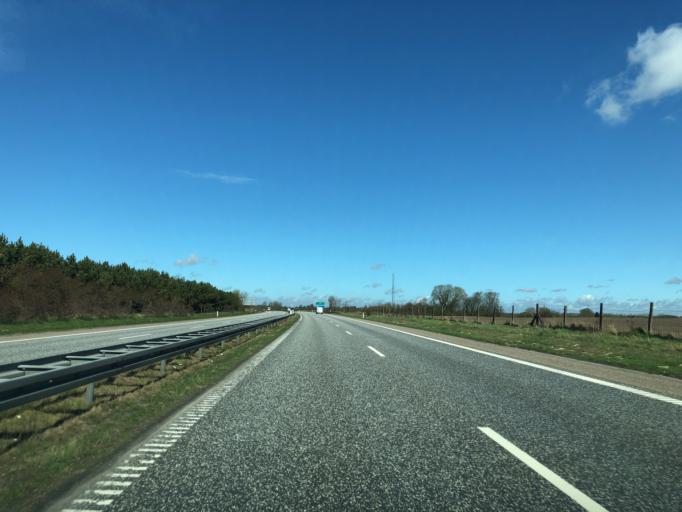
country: DK
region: North Denmark
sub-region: Alborg Kommune
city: Vestbjerg
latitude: 57.1459
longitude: 9.9460
